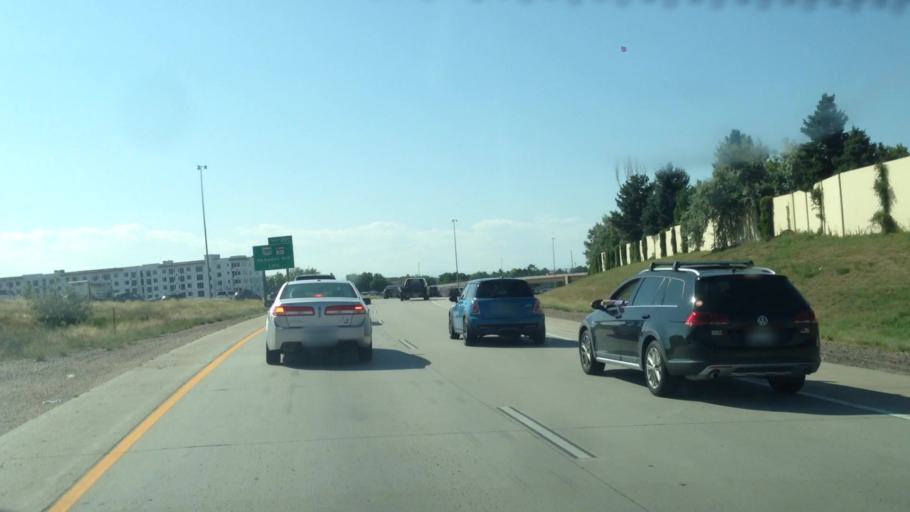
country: US
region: Colorado
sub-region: Arapahoe County
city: Greenwood Village
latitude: 39.6361
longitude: -104.9071
